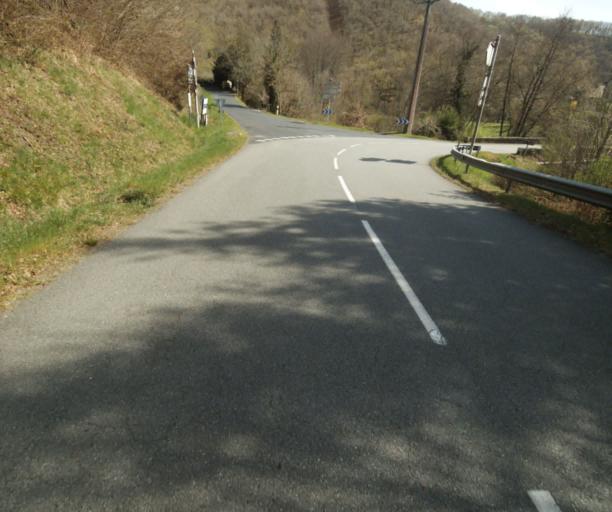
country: FR
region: Limousin
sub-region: Departement de la Correze
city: Naves
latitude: 45.3385
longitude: 1.7920
